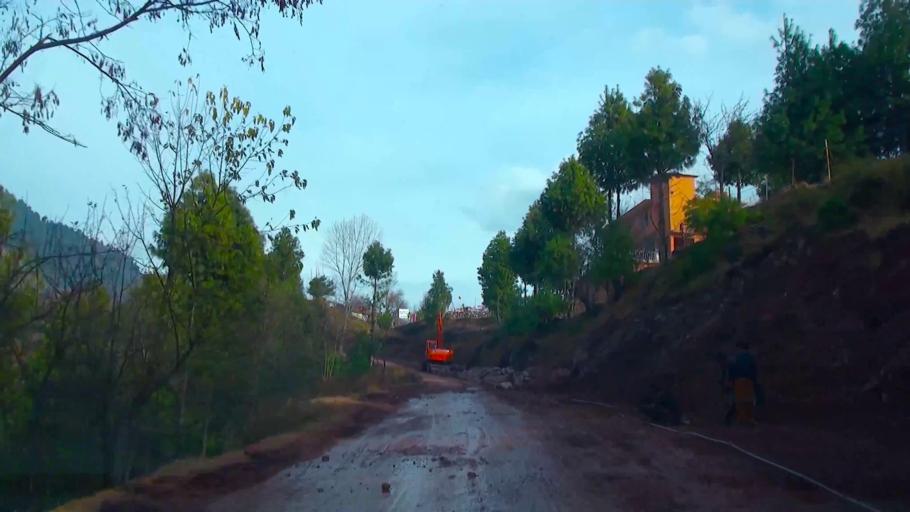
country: PK
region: Azad Kashmir
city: Muzaffarabad
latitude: 34.3700
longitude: 73.5124
